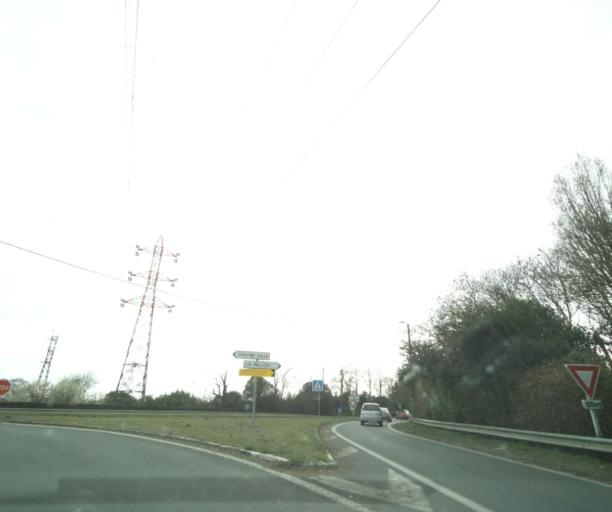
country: FR
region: Poitou-Charentes
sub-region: Departement de la Charente-Maritime
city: La Rochelle
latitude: 46.1653
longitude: -1.1939
